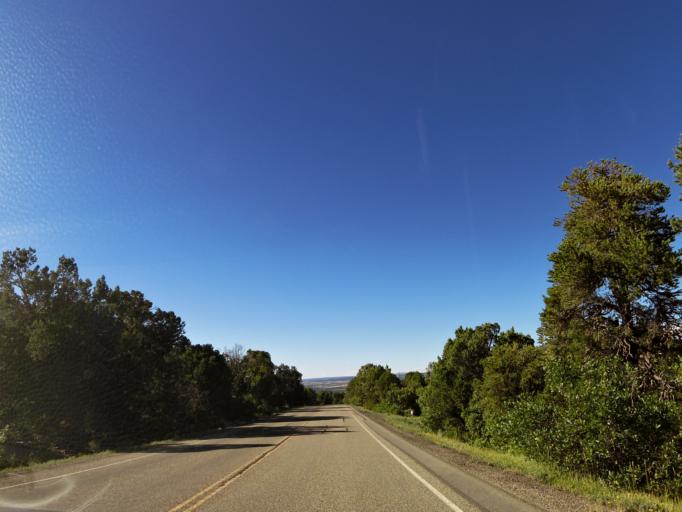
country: US
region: Colorado
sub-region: Montezuma County
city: Mancos
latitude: 37.3260
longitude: -108.4170
